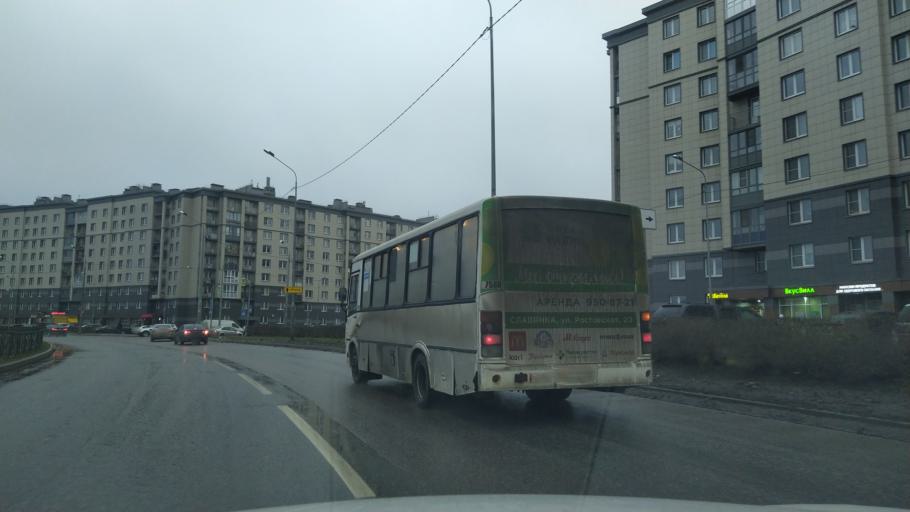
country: RU
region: St.-Petersburg
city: Tyarlevo
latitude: 59.7417
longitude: 30.4708
